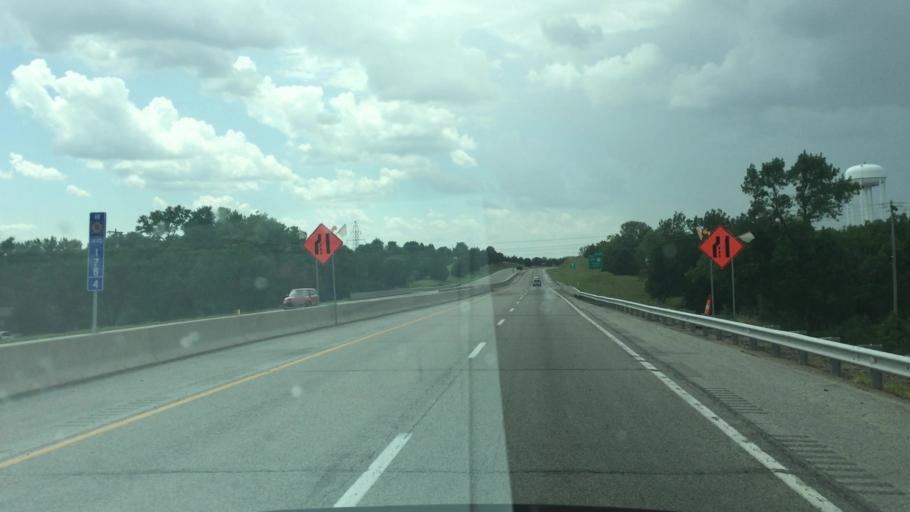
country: US
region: Kansas
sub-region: Shawnee County
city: Topeka
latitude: 38.9953
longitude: -95.6695
